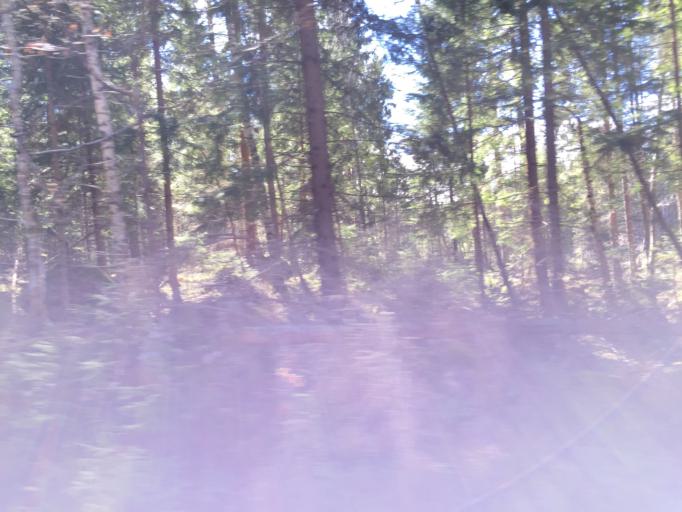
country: SE
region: OEstergoetland
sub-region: Finspangs Kommun
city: Finspang
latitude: 58.8885
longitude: 15.7355
